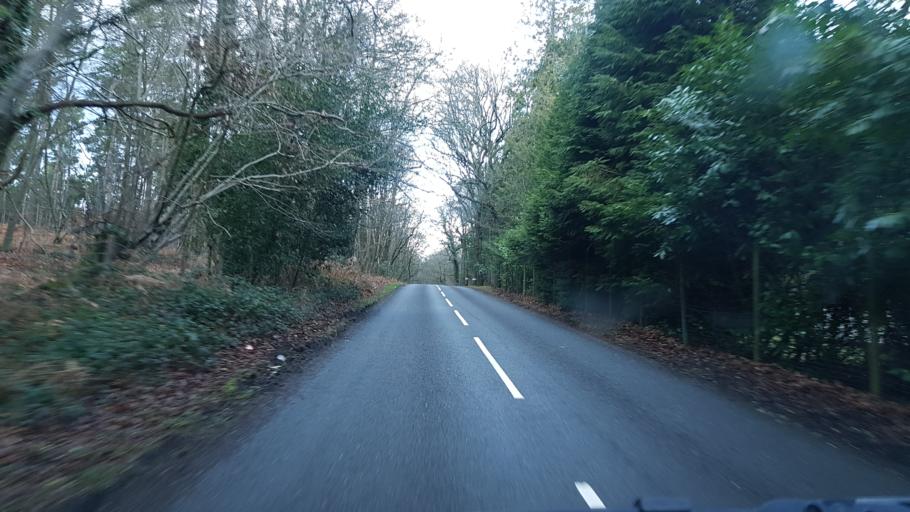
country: GB
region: England
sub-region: Surrey
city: Elstead
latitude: 51.1942
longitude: -0.7157
